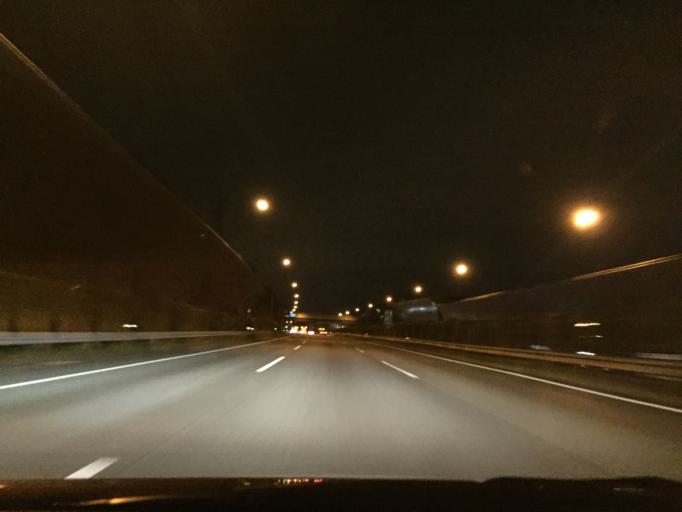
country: JP
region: Kanagawa
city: Isehara
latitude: 35.3814
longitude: 139.2709
